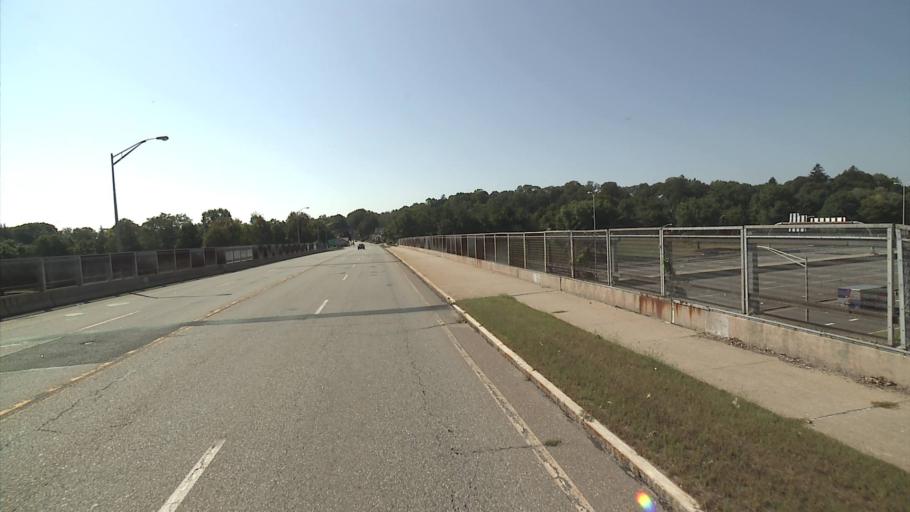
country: US
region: Connecticut
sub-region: New London County
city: New London
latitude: 41.3669
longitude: -72.1086
